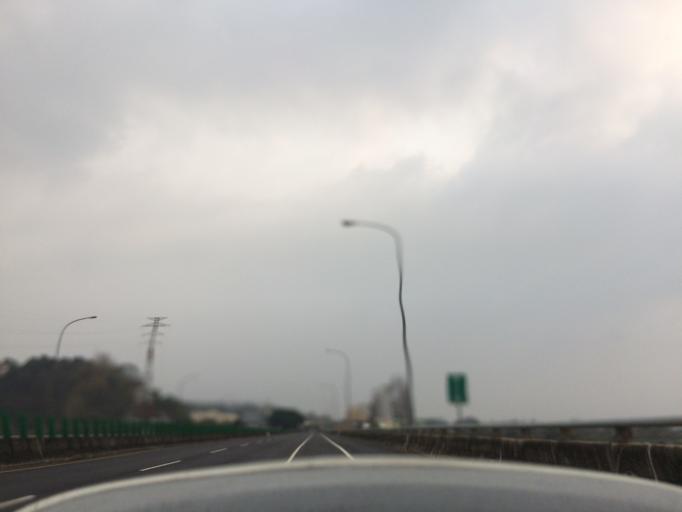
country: TW
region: Taiwan
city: Zhongxing New Village
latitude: 24.0081
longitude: 120.6951
